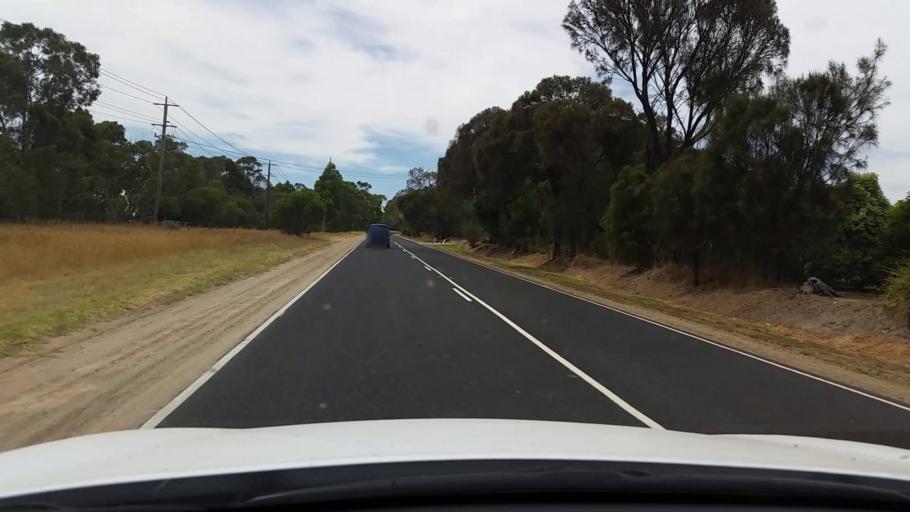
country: AU
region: Victoria
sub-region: Mornington Peninsula
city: Safety Beach
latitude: -38.3086
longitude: 145.0323
